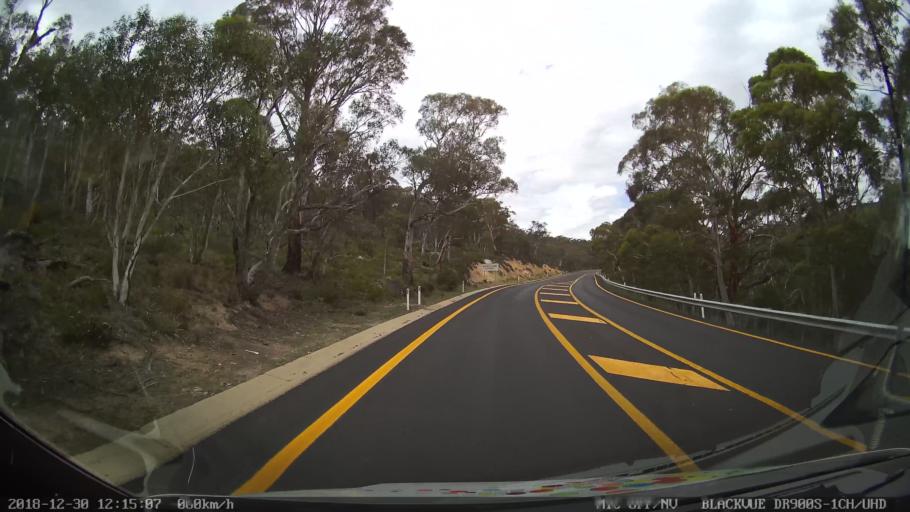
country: AU
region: New South Wales
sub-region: Snowy River
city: Jindabyne
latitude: -36.3443
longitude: 148.5746
